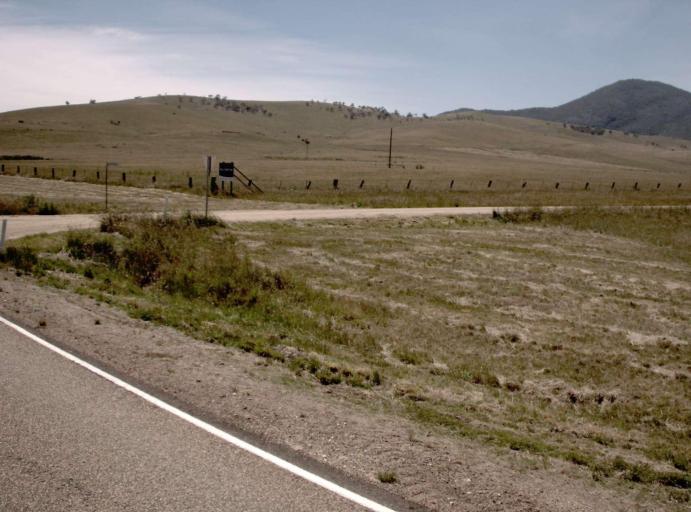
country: AU
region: Victoria
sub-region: Alpine
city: Mount Beauty
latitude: -36.9968
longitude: 147.6795
